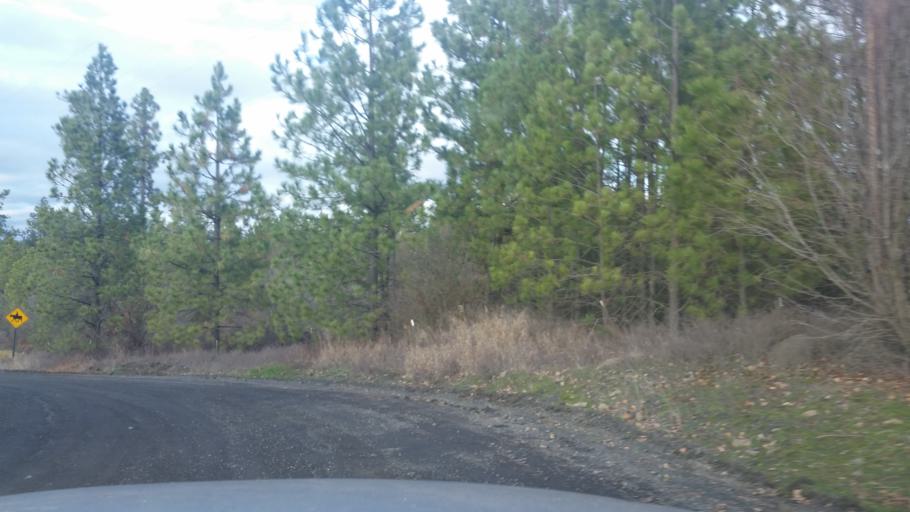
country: US
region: Washington
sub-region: Spokane County
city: Cheney
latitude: 47.4260
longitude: -117.4645
